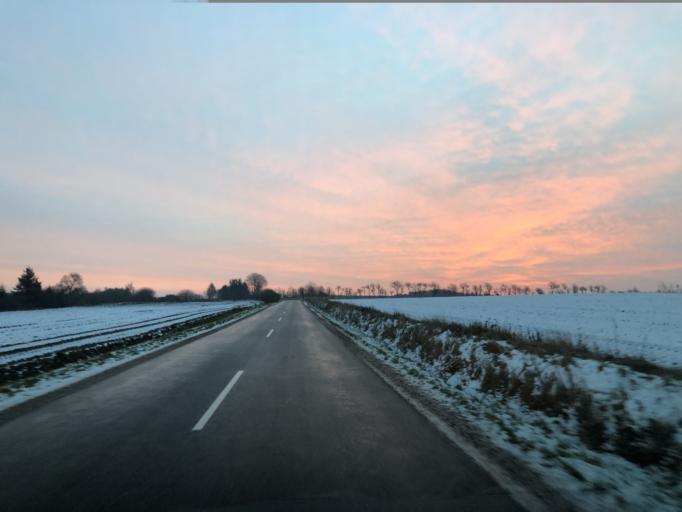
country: DK
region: Central Jutland
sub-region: Holstebro Kommune
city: Ulfborg
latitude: 56.2010
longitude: 8.4433
